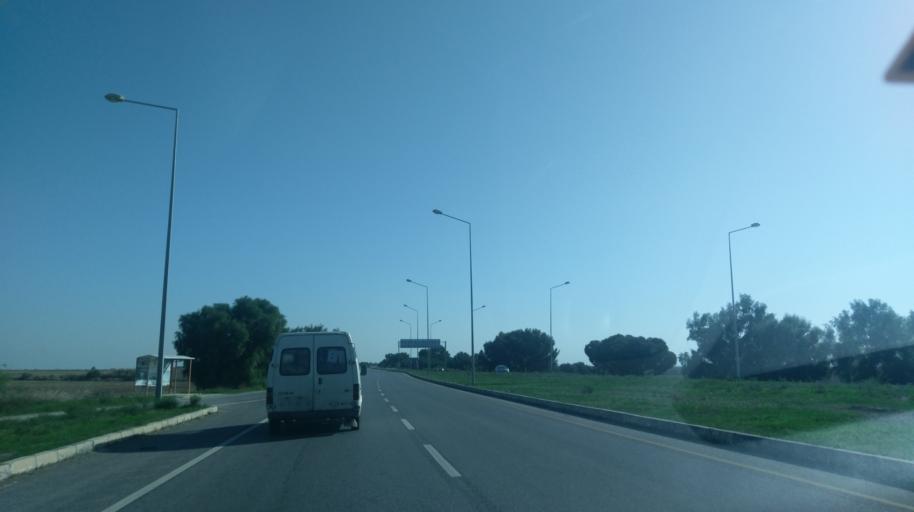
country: CY
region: Ammochostos
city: Lefkonoiko
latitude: 35.1830
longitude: 33.7011
